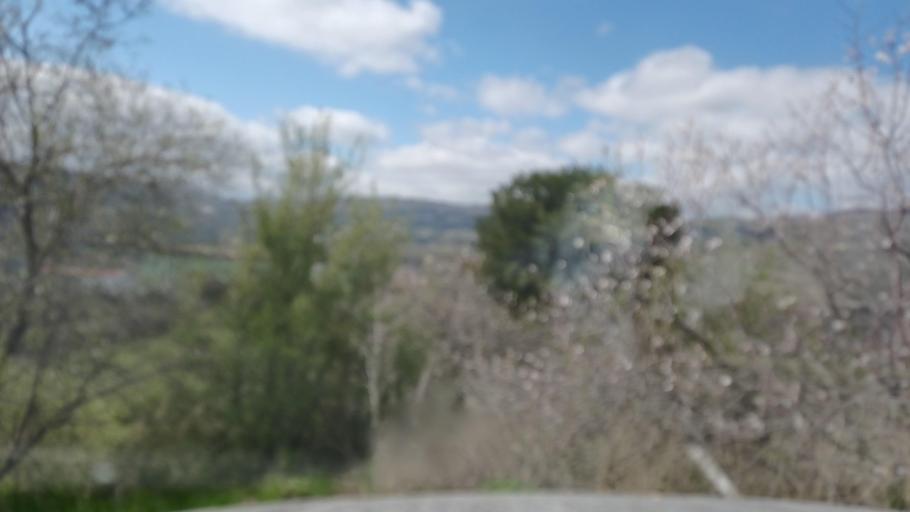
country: CY
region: Limassol
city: Pachna
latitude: 34.8441
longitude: 32.7334
